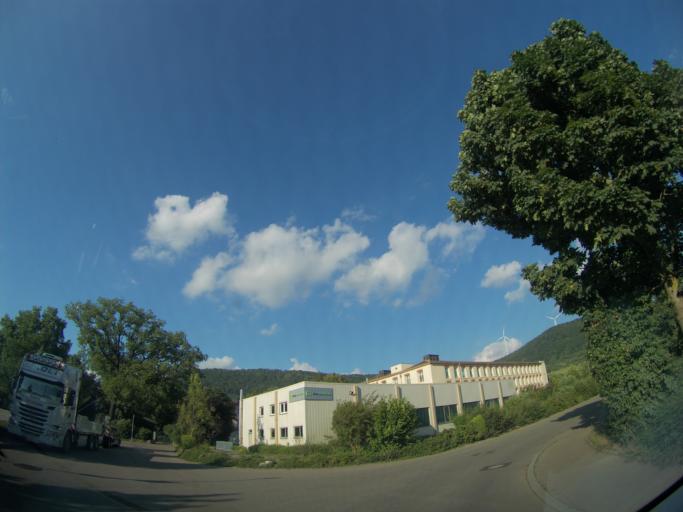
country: DE
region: Baden-Wuerttemberg
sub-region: Regierungsbezirk Stuttgart
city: Kuchen
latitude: 48.6465
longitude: 9.7903
